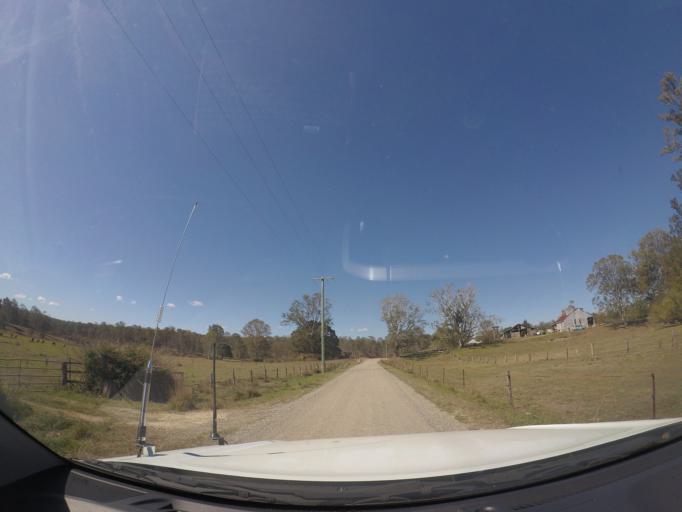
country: AU
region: Queensland
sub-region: Ipswich
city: Springfield Lakes
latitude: -27.7470
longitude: 152.9112
